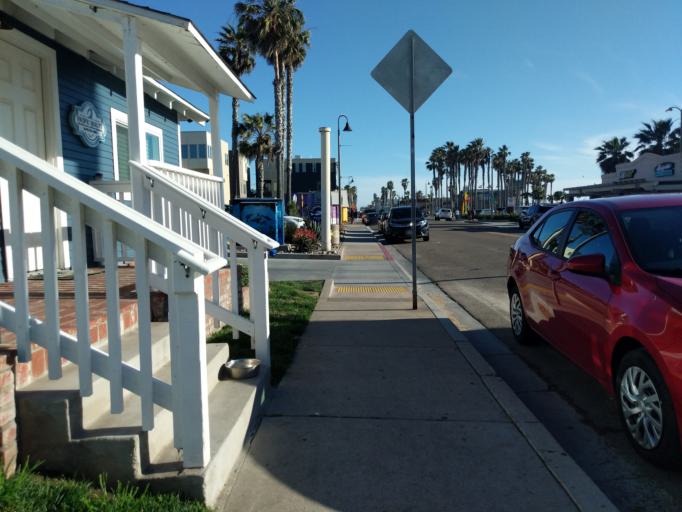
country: US
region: California
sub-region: San Diego County
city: Imperial Beach
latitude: 32.5808
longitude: -117.1317
